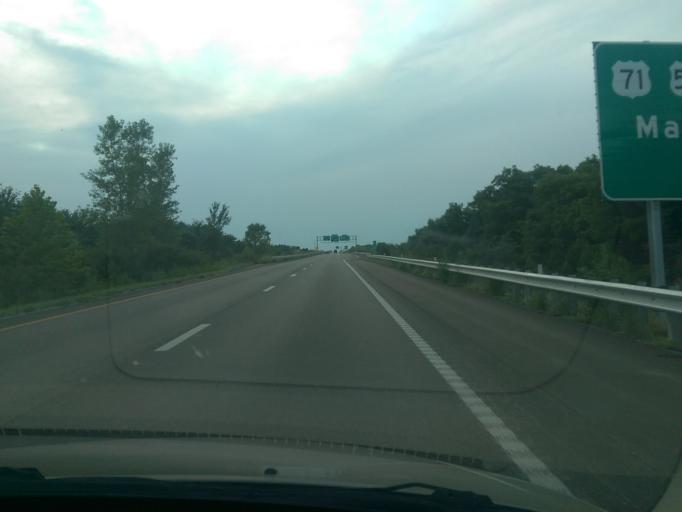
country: US
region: Missouri
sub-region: Andrew County
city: Country Club Village
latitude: 39.8837
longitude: -94.8517
